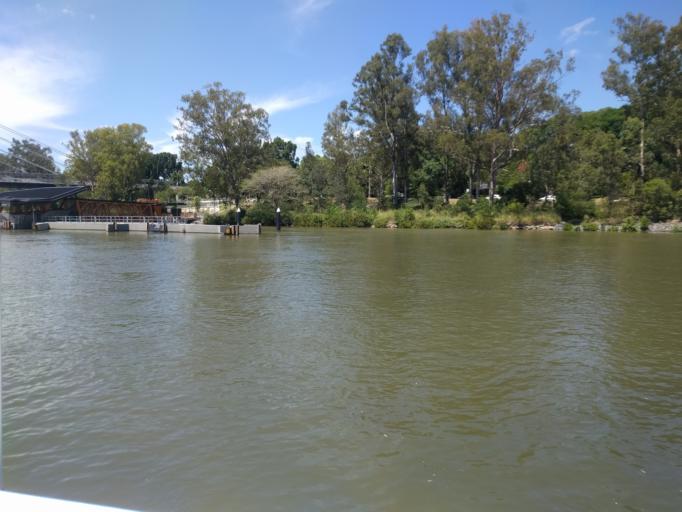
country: AU
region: Queensland
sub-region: Brisbane
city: South Brisbane
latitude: -27.4957
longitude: 153.0194
